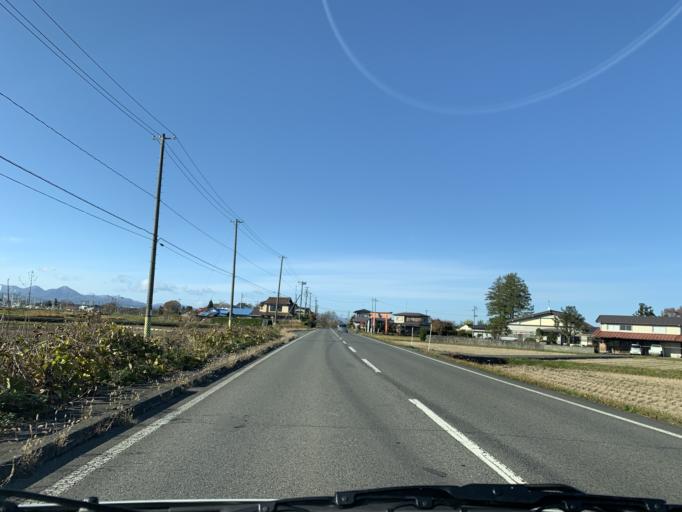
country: JP
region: Iwate
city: Mizusawa
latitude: 39.1807
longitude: 141.1323
